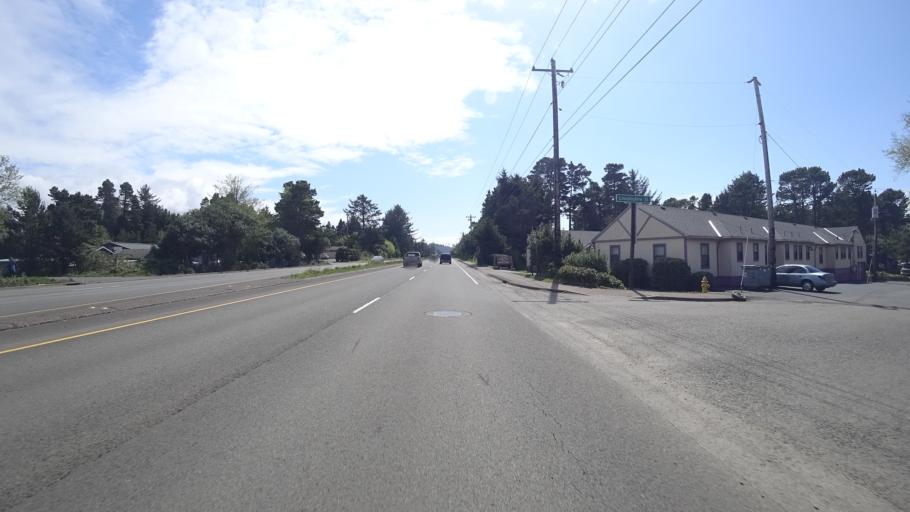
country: US
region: Oregon
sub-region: Lincoln County
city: Lincoln Beach
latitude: 44.8559
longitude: -124.0411
